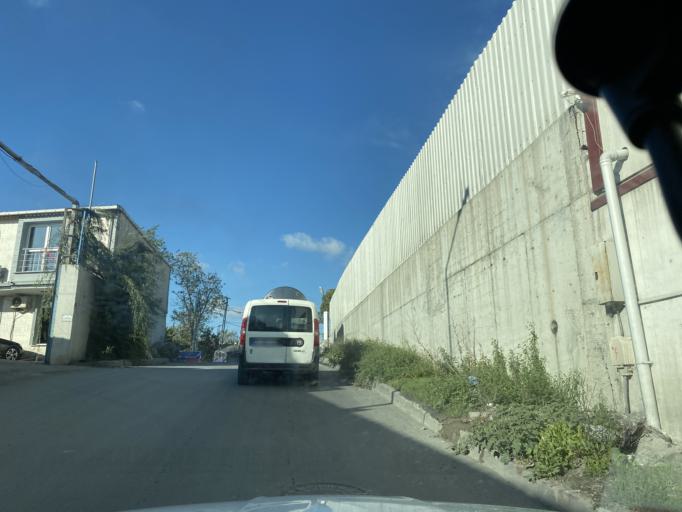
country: TR
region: Istanbul
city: Esenyurt
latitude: 41.0542
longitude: 28.6477
